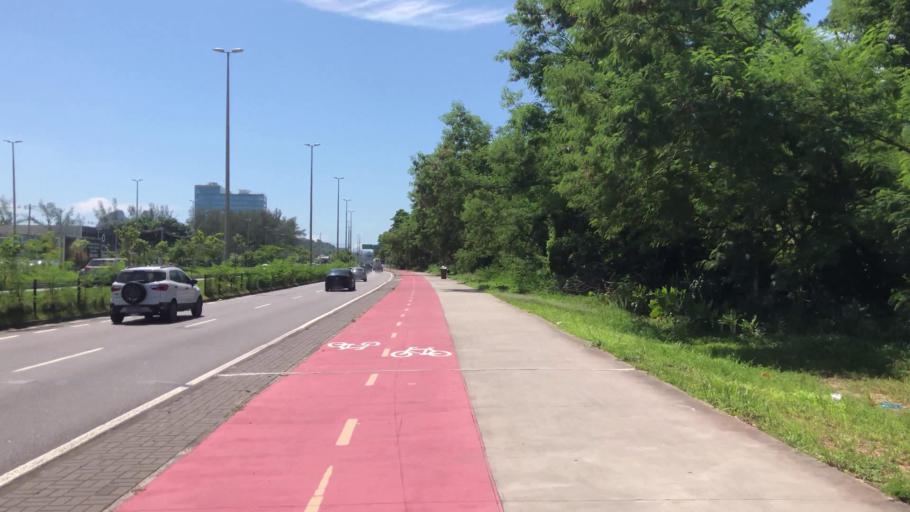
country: BR
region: Rio de Janeiro
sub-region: Nilopolis
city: Nilopolis
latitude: -22.9735
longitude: -43.4030
